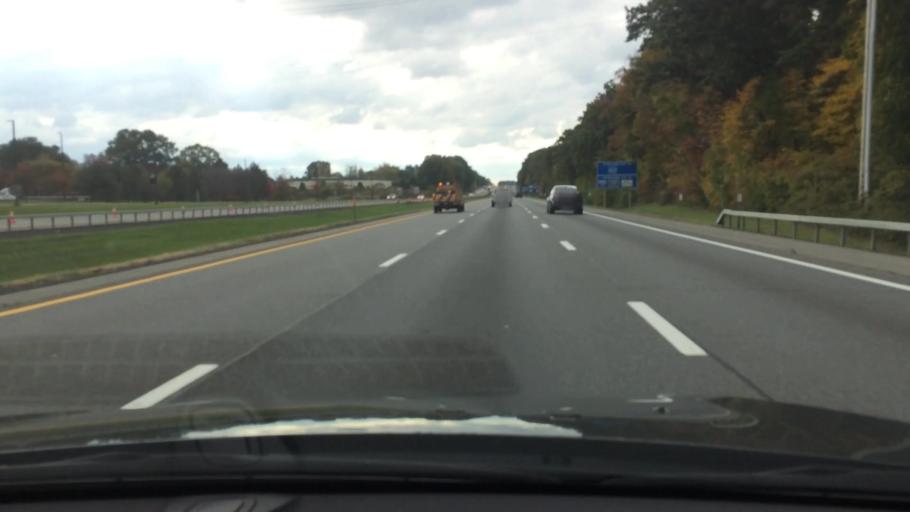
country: US
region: New York
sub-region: Saratoga County
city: Country Knolls
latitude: 42.8774
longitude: -73.7779
